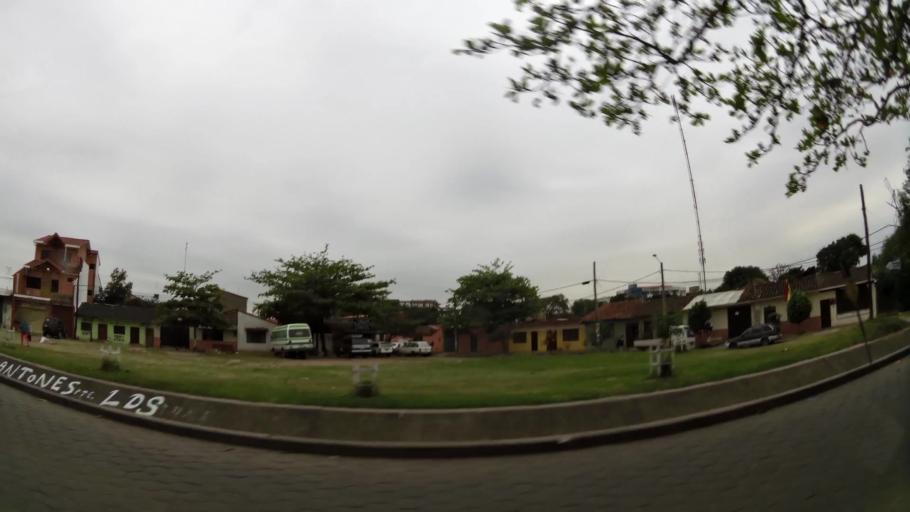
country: BO
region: Santa Cruz
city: Santa Cruz de la Sierra
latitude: -17.7787
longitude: -63.1981
